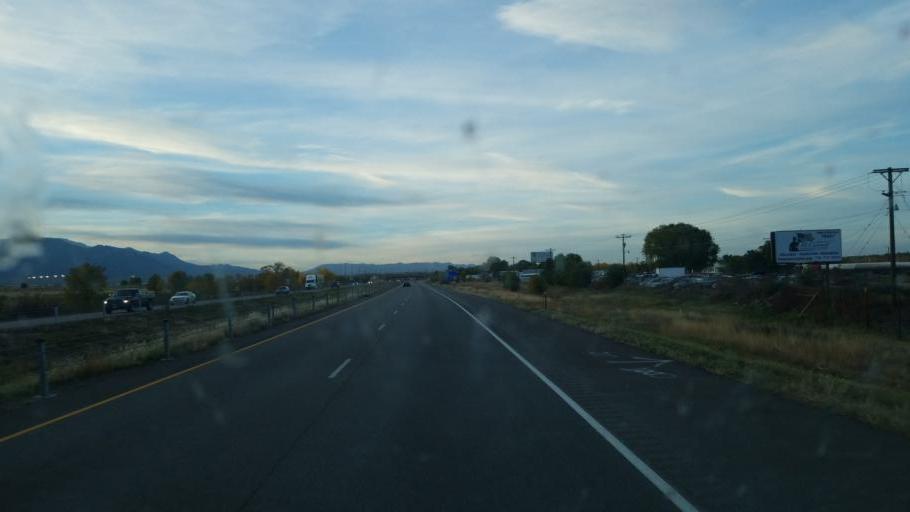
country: US
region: Colorado
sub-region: El Paso County
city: Fountain
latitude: 38.6646
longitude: -104.7023
